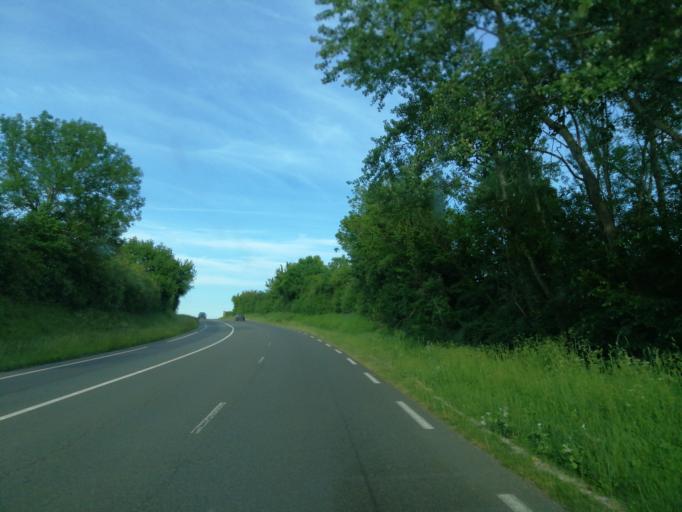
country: FR
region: Centre
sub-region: Departement d'Eure-et-Loir
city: Gallardon
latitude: 48.5014
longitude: 1.7273
